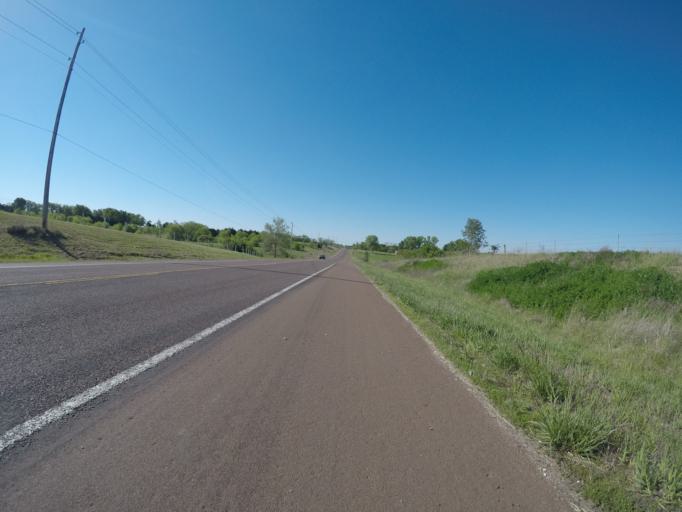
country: US
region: Kansas
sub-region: Douglas County
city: Lawrence
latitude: 39.0198
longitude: -95.3914
